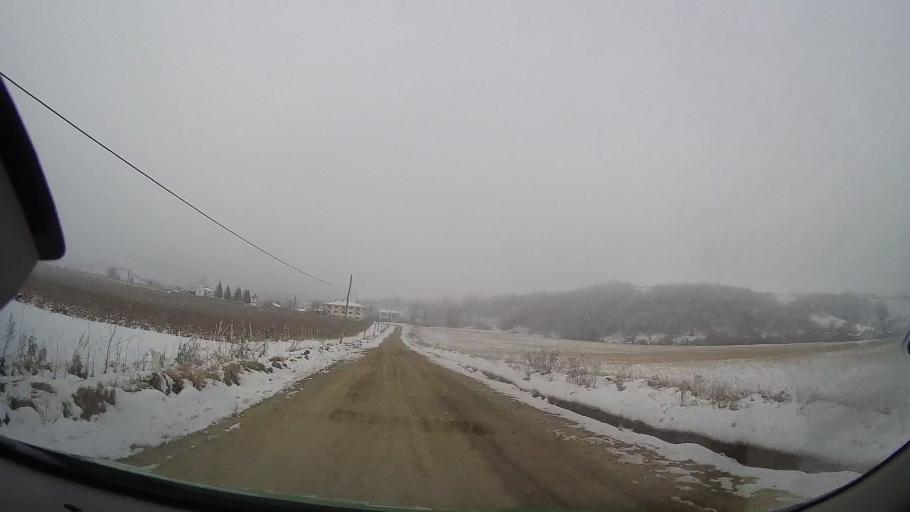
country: RO
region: Bacau
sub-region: Comuna Vultureni
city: Vultureni
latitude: 46.3759
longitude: 27.2801
